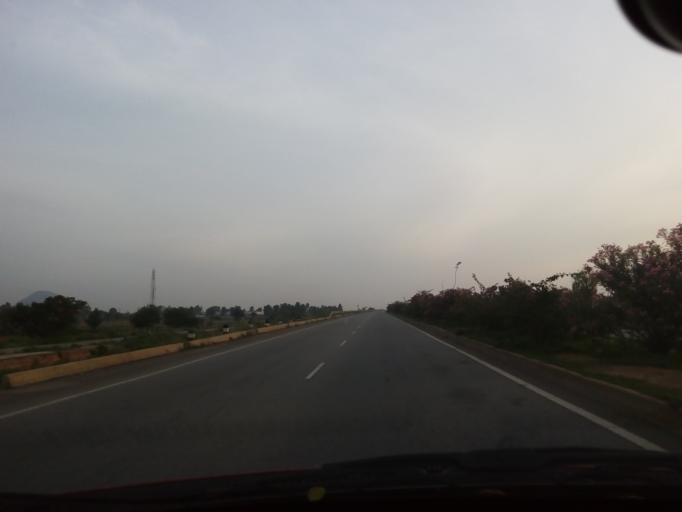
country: IN
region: Karnataka
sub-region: Chikkaballapur
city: Chik Ballapur
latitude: 13.3473
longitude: 77.7256
